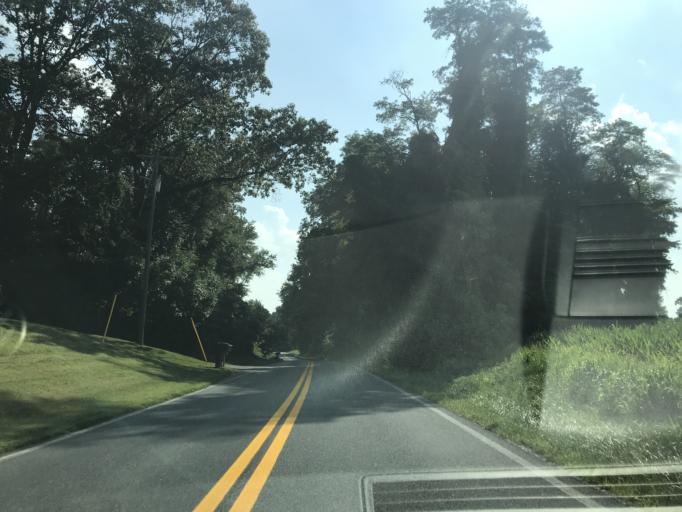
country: US
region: Maryland
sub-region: Carroll County
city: Manchester
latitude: 39.6373
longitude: -76.9468
